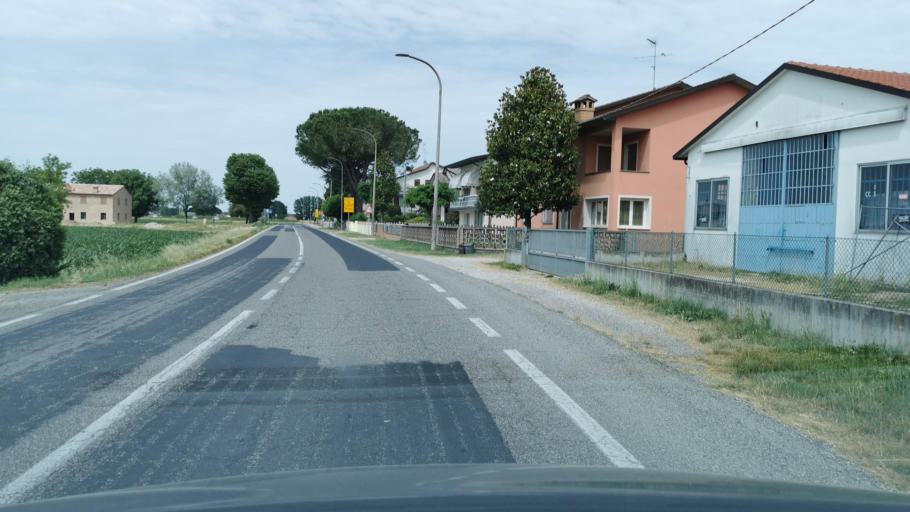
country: IT
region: Emilia-Romagna
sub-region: Provincia di Ravenna
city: Savarna-Conventella
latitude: 44.5026
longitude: 12.0998
